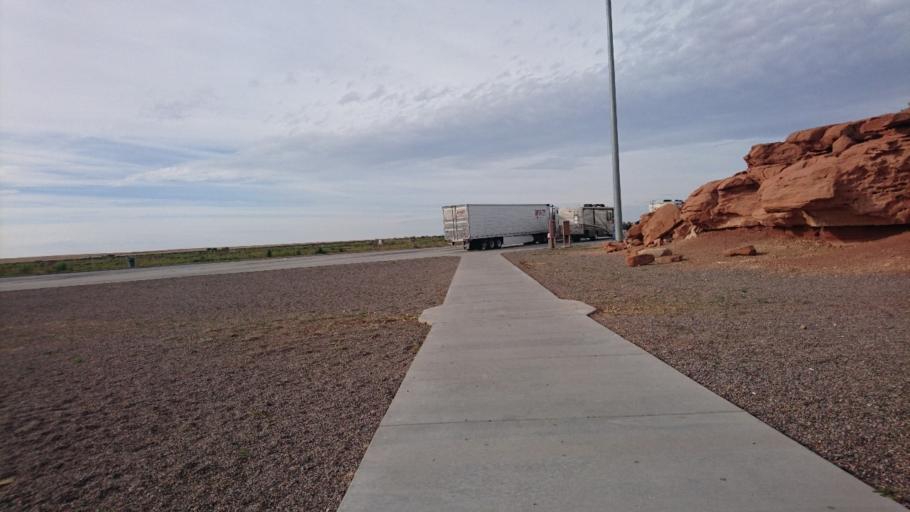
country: US
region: Arizona
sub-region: Coconino County
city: LeChee
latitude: 35.1039
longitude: -110.9924
